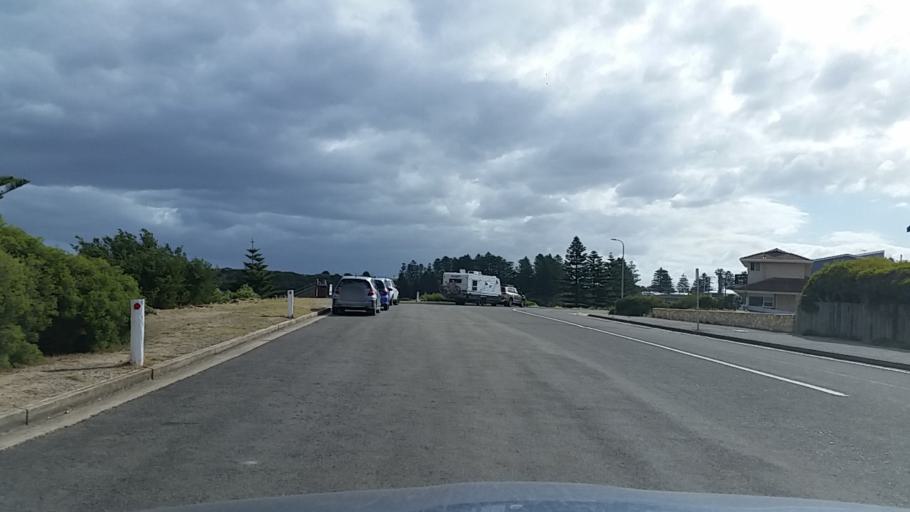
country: AU
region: South Australia
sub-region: Alexandrina
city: Port Elliot
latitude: -35.5314
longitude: 138.6881
